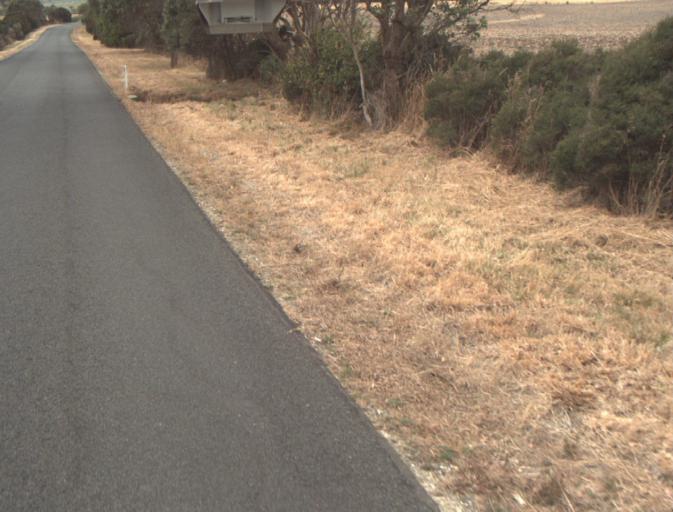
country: AU
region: Tasmania
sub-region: Launceston
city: Mayfield
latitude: -41.2086
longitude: 147.0597
